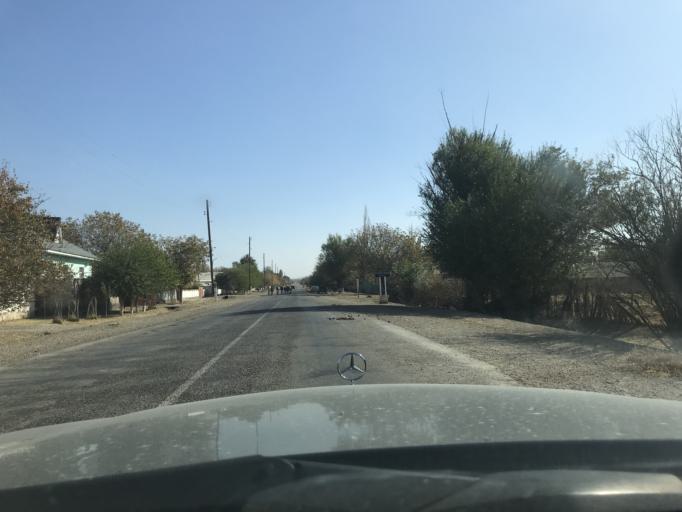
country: KZ
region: Ongtustik Qazaqstan
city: Sastobe
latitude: 42.5464
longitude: 69.9206
